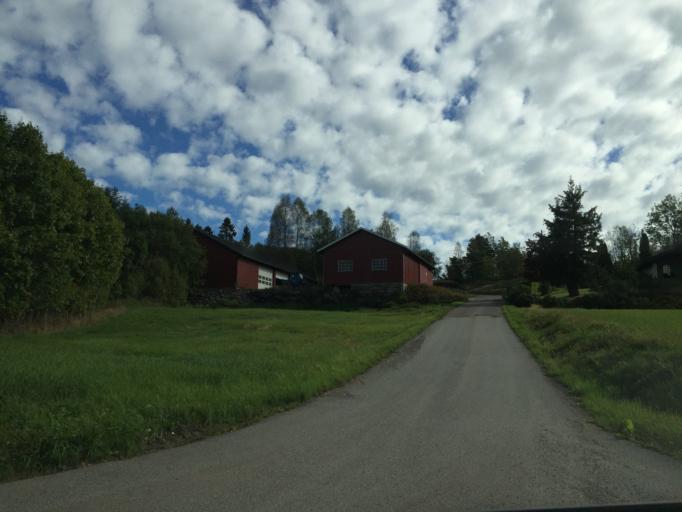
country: NO
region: Vestfold
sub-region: Holmestrand
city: Gullhaug
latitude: 59.4699
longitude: 10.1949
